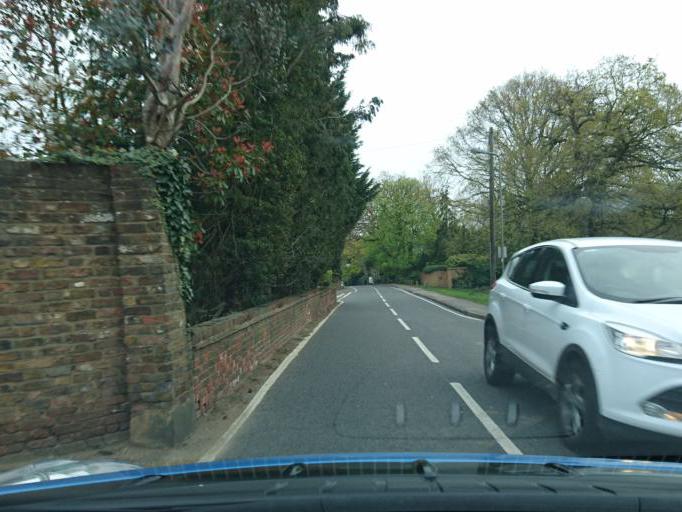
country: GB
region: England
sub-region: Greater London
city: Barnet
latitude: 51.6349
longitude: -0.1993
